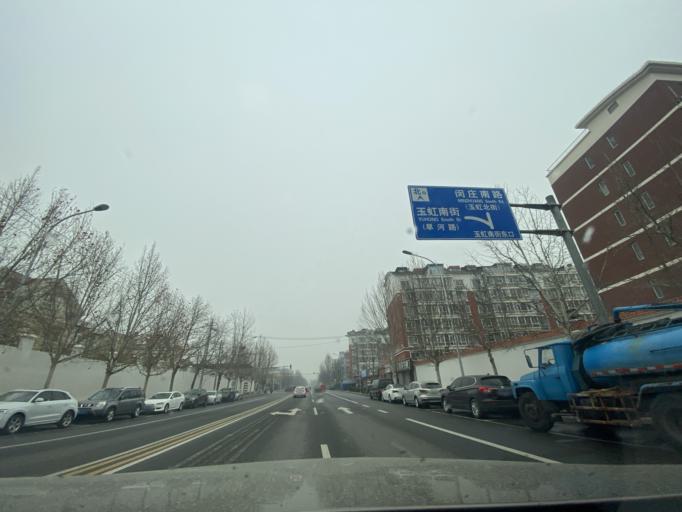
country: CN
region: Beijing
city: Sijiqing
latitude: 39.9613
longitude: 116.2421
